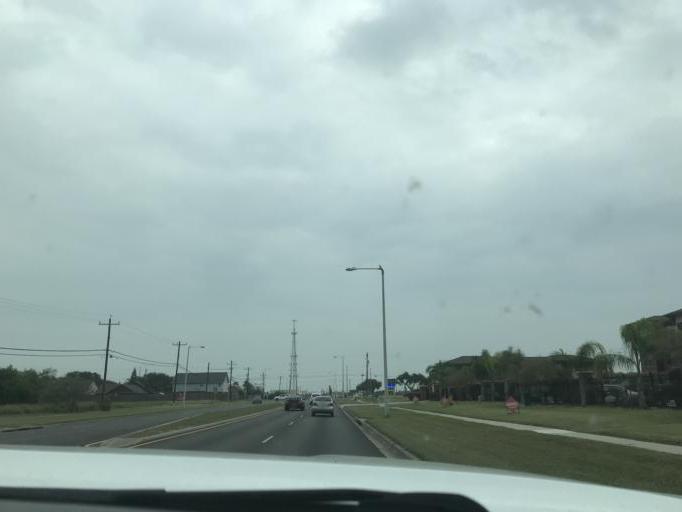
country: US
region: Texas
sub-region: Nueces County
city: Corpus Christi
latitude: 27.6736
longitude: -97.3601
